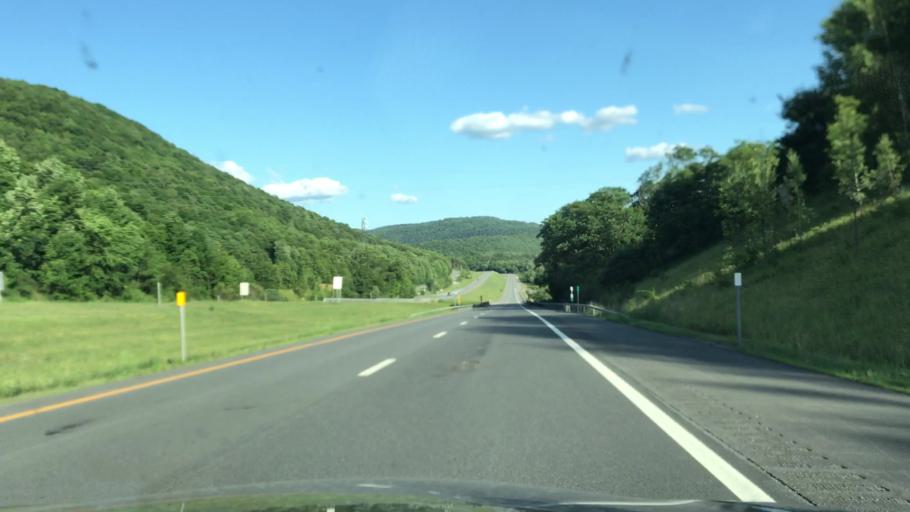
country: US
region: New York
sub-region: Sullivan County
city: Livingston Manor
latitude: 41.9604
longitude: -74.9932
